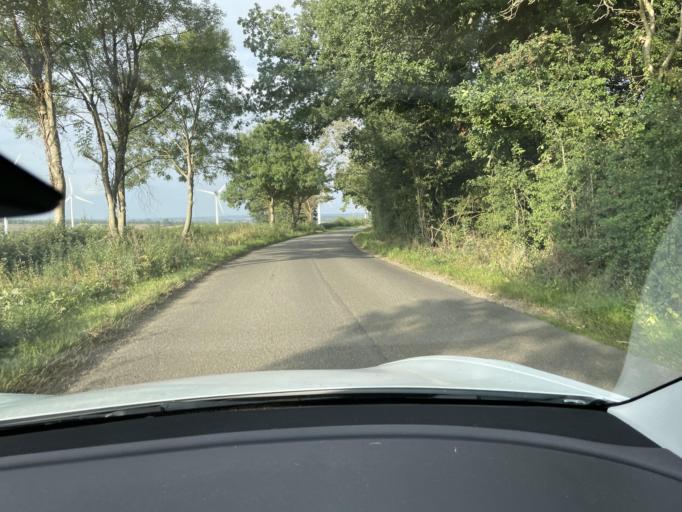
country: GB
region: England
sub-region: Northamptonshire
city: Brixworth
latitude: 52.3929
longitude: -0.9498
